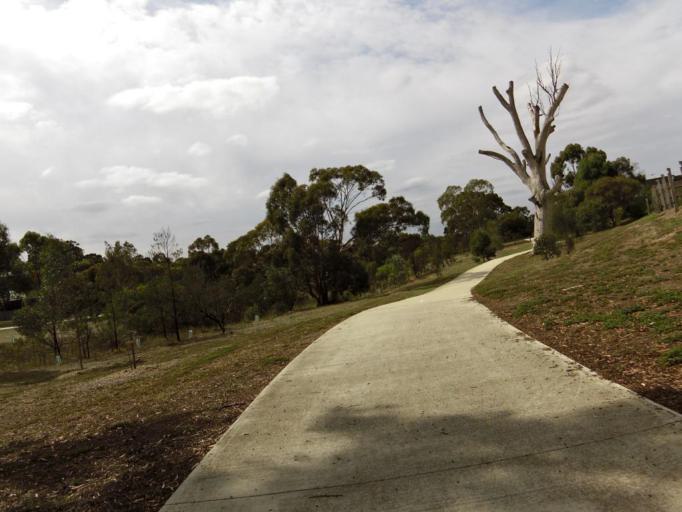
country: AU
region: Victoria
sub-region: Hume
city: Sunbury
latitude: -37.5689
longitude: 144.7086
